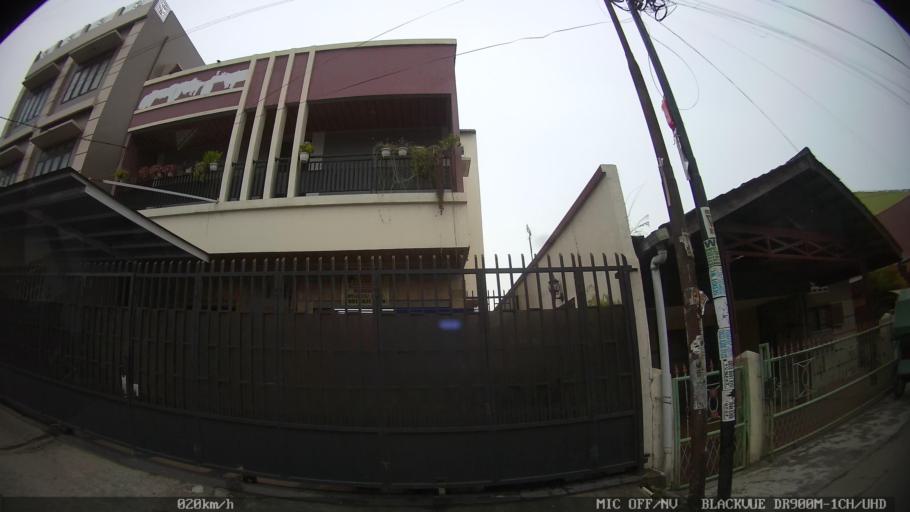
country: ID
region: North Sumatra
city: Deli Tua
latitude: 3.5439
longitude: 98.6996
